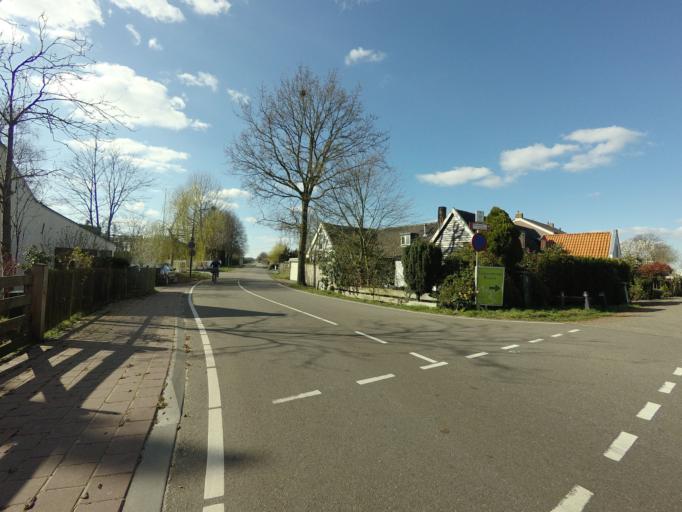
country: NL
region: North Holland
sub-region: Gemeente Wijdemeren
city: Kortenhoef
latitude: 52.2593
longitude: 5.1243
